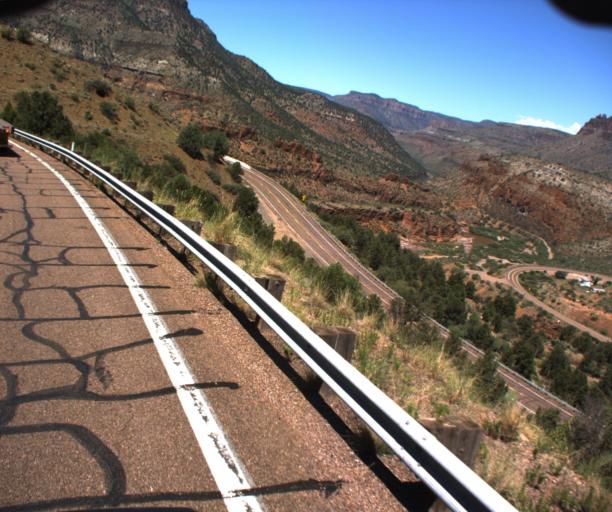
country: US
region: Arizona
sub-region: Navajo County
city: Cibecue
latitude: 33.7945
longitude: -110.5029
